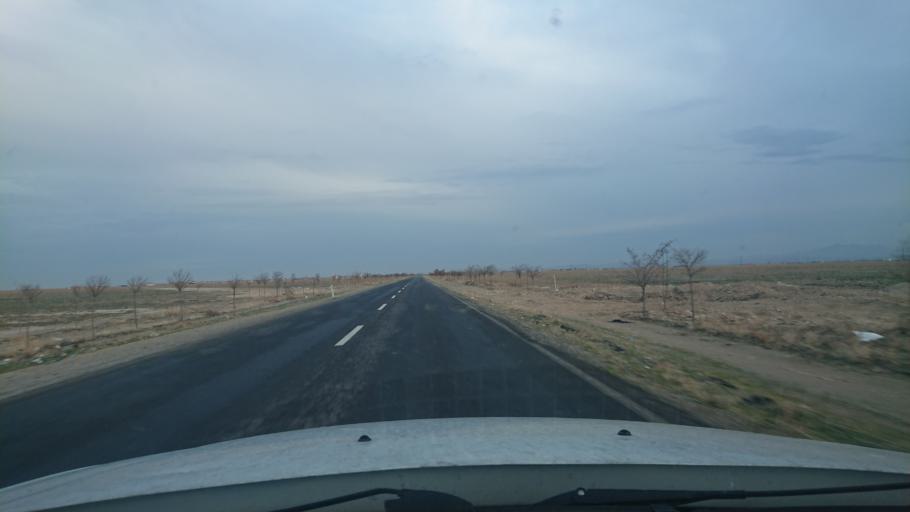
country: TR
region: Aksaray
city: Yesilova
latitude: 38.3140
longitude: 33.7538
